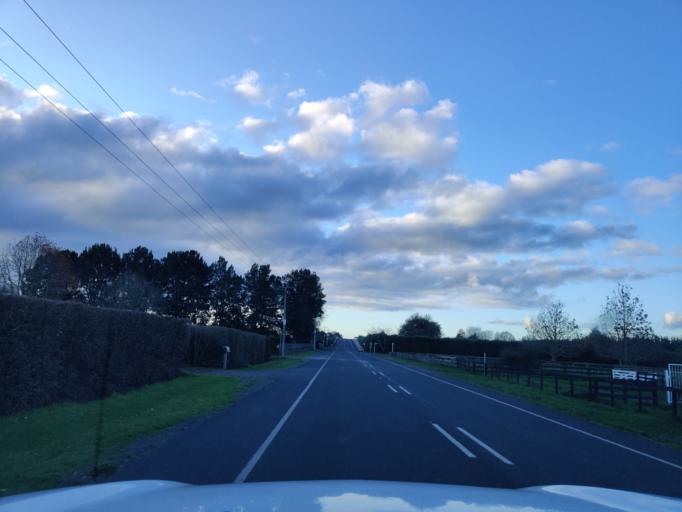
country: NZ
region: Waikato
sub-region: Waipa District
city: Cambridge
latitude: -37.8723
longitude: 175.4389
